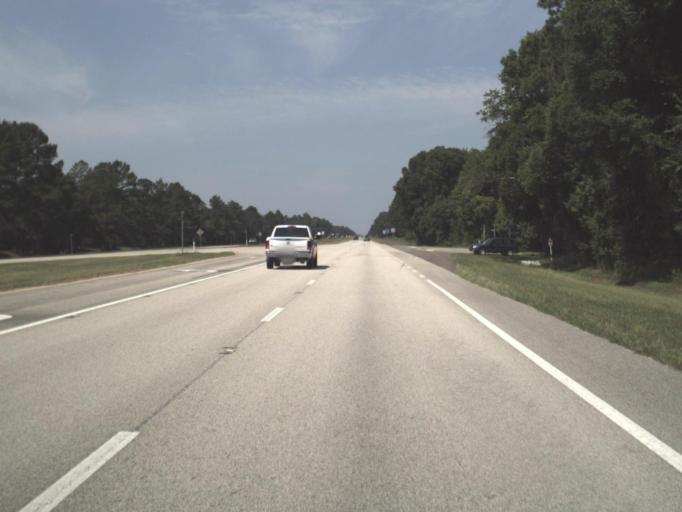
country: US
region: Florida
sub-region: Alachua County
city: Waldo
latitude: 29.7845
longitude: -82.1750
